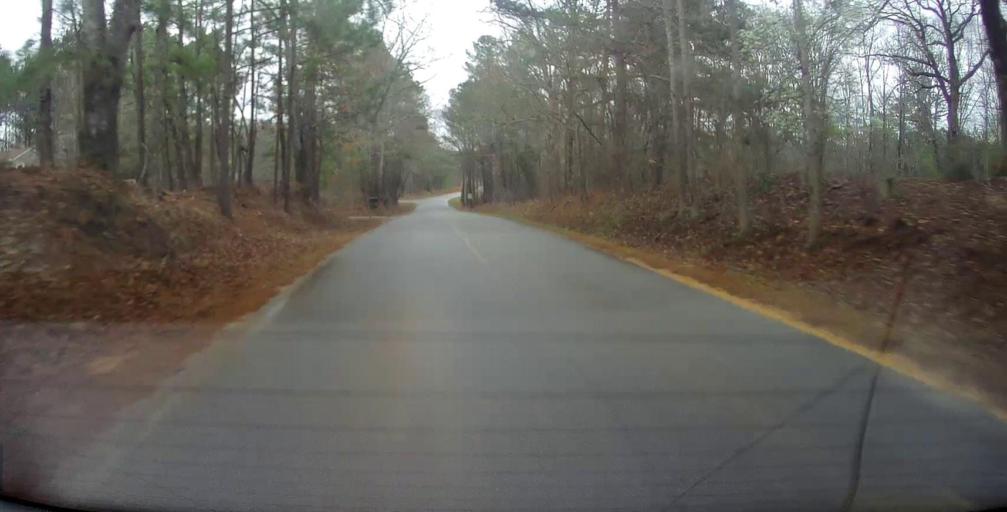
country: US
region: Georgia
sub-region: Monroe County
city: Forsyth
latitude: 33.0872
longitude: -83.9319
